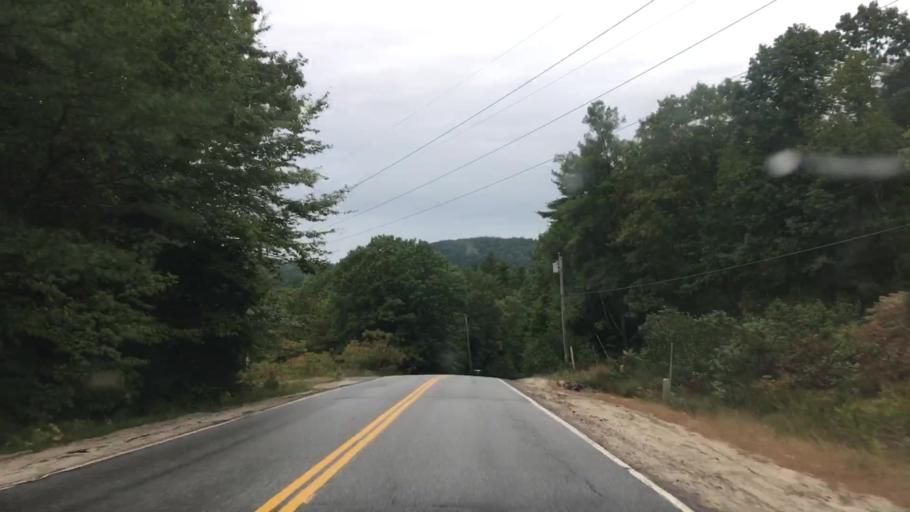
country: US
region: Maine
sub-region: Cumberland County
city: Raymond
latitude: 43.9448
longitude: -70.4601
